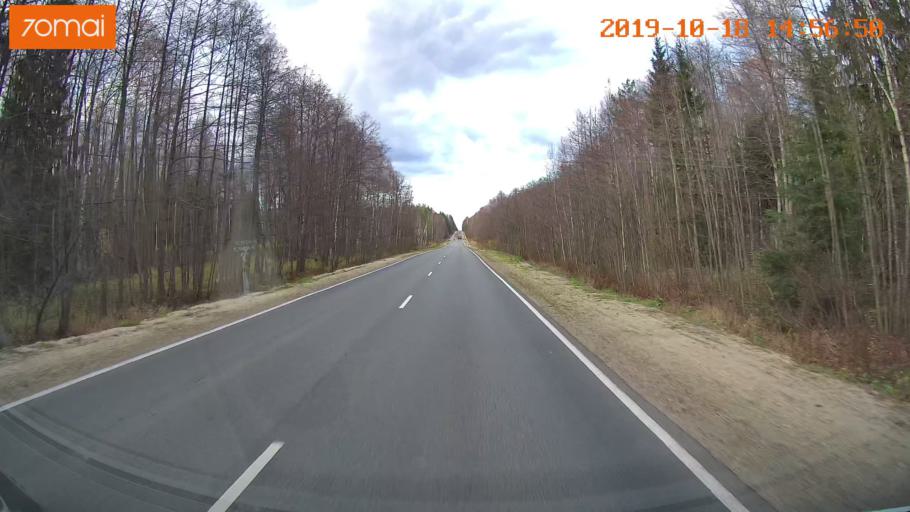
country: RU
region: Vladimir
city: Kurlovo
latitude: 55.4706
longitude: 40.5851
